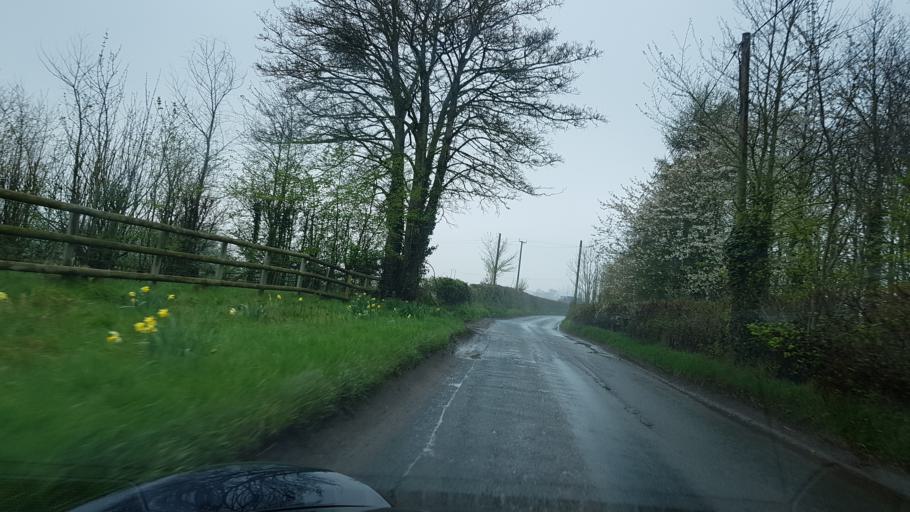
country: GB
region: England
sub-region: Herefordshire
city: Sellack
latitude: 51.9243
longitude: -2.6209
